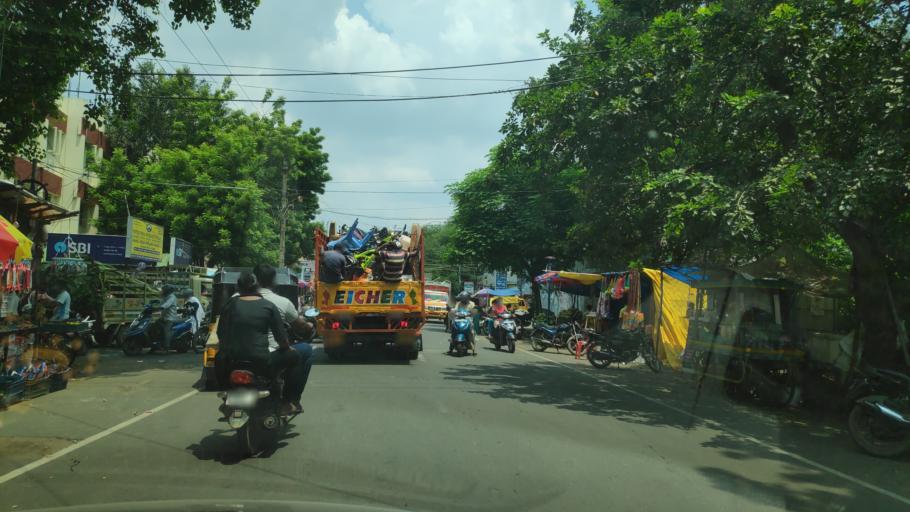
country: IN
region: Tamil Nadu
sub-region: Thiruvallur
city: Ambattur
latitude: 13.1192
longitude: 80.1507
